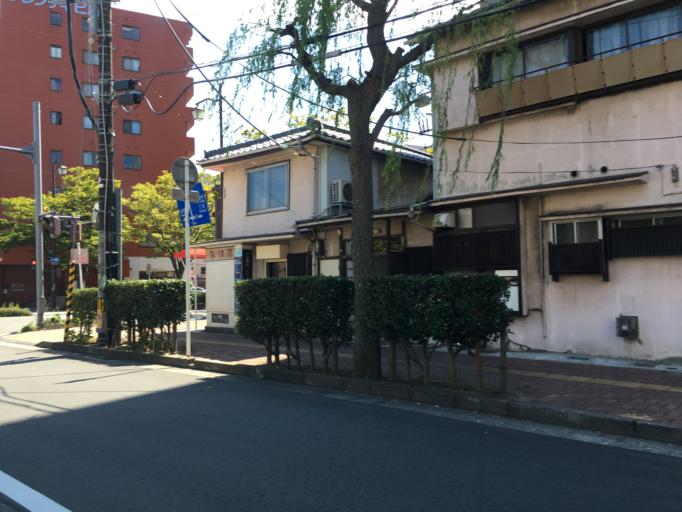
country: JP
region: Niigata
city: Niigata-shi
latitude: 37.9228
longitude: 139.0491
